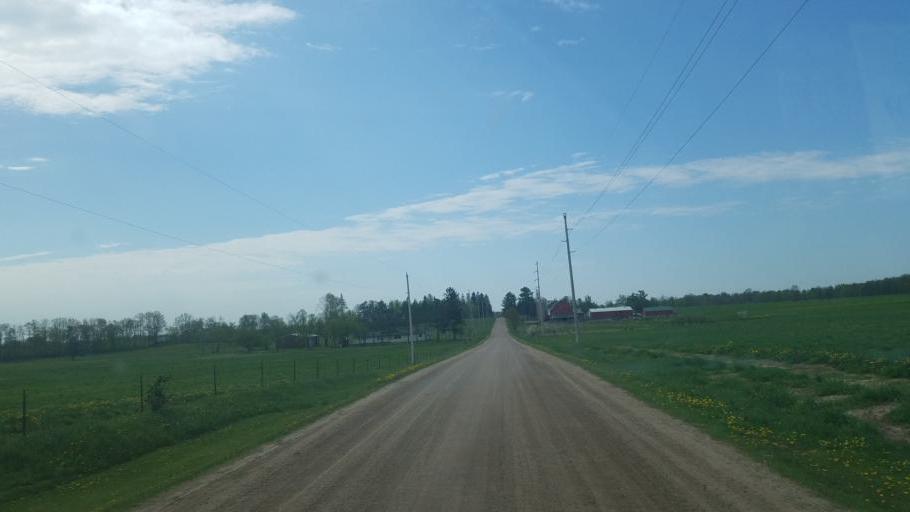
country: US
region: Wisconsin
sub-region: Marathon County
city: Spencer
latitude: 44.6247
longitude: -90.3766
